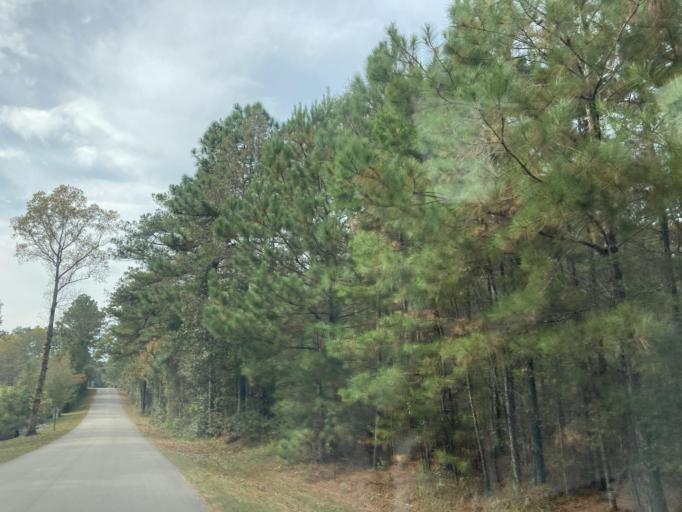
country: US
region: Mississippi
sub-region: Lamar County
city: West Hattiesburg
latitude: 31.3246
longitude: -89.4320
